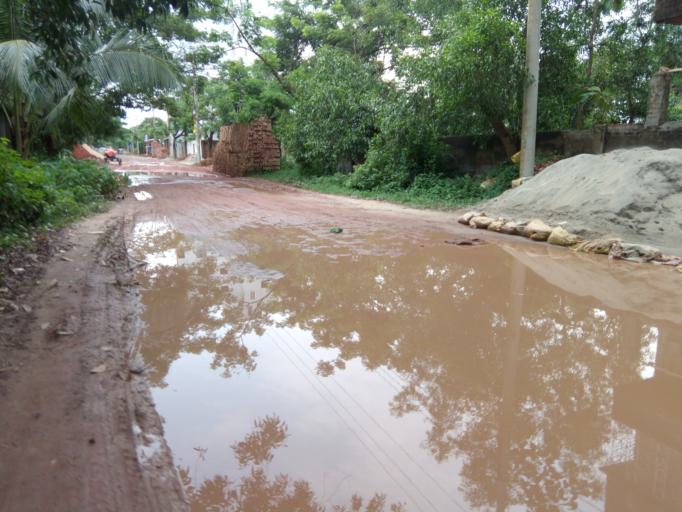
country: BD
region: Dhaka
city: Azimpur
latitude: 23.7523
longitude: 90.3456
